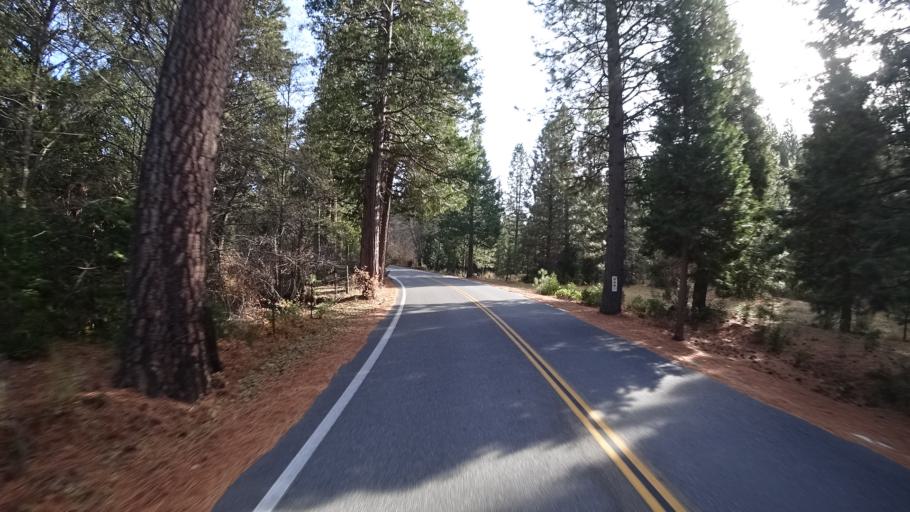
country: US
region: California
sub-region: Siskiyou County
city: Weed
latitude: 41.4042
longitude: -122.4280
